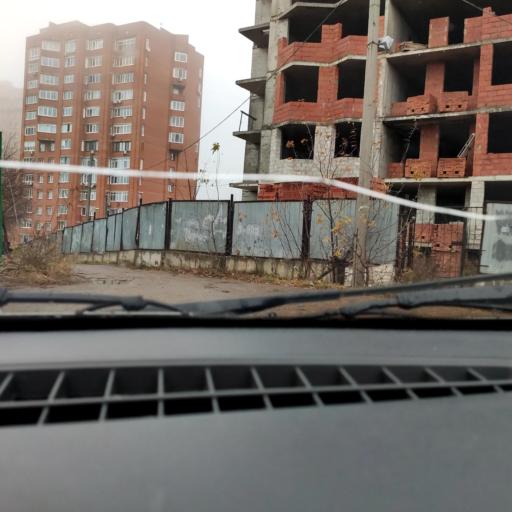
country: RU
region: Bashkortostan
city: Ufa
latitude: 54.7027
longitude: 55.9846
